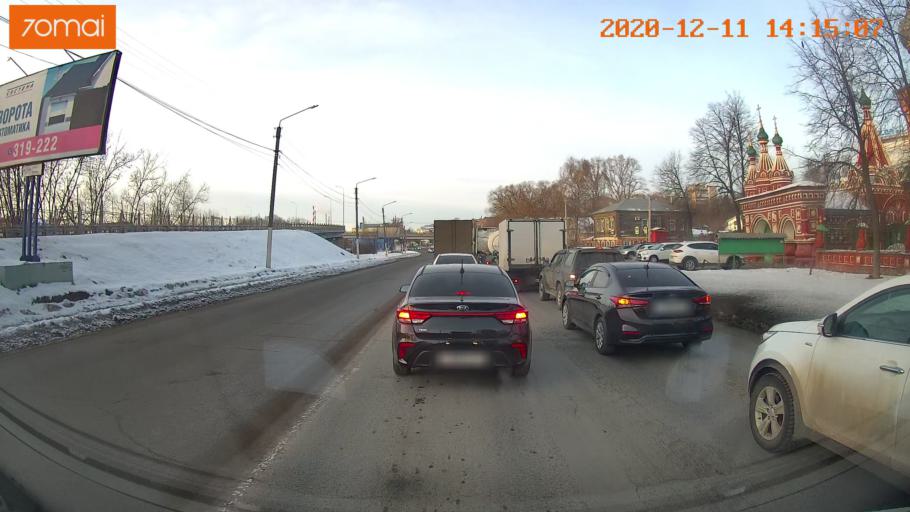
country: RU
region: Kostroma
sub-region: Kostromskoy Rayon
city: Kostroma
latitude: 57.7552
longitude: 40.9481
